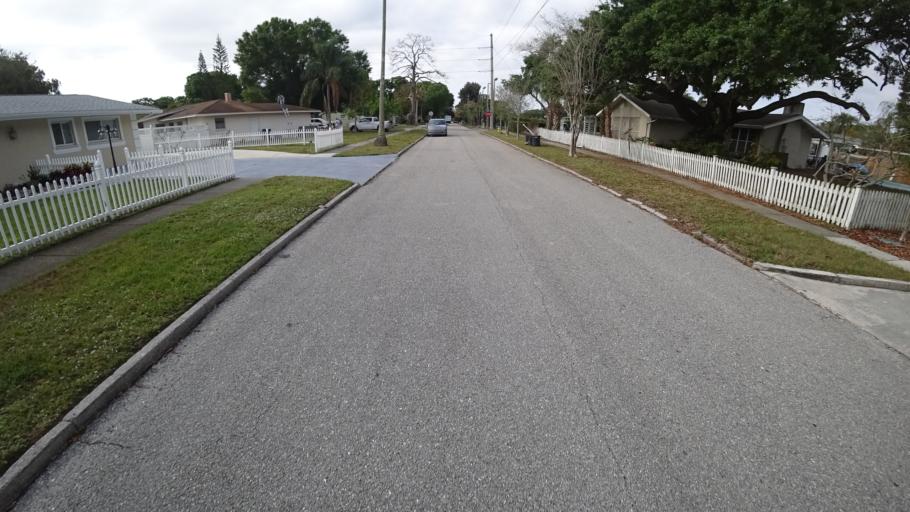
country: US
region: Florida
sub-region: Manatee County
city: West Bradenton
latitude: 27.4927
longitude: -82.6060
